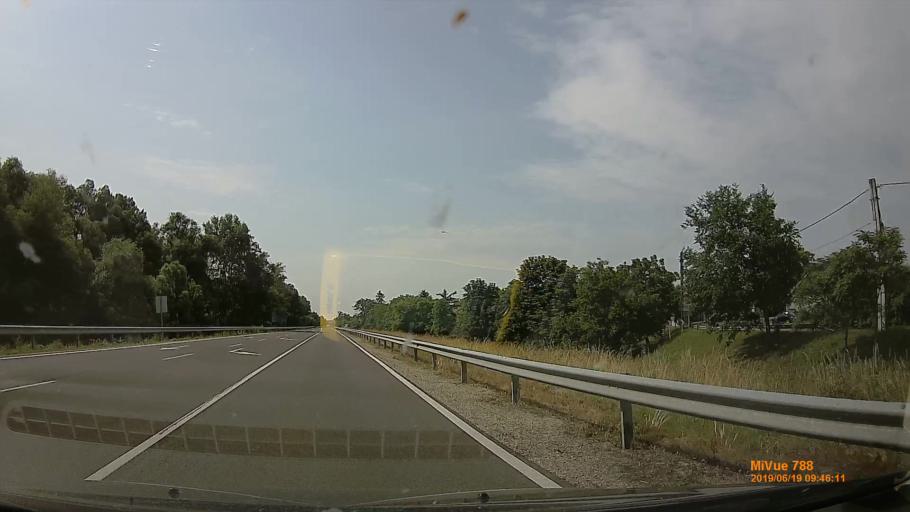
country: HU
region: Fejer
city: Adony
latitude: 47.1222
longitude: 18.8684
